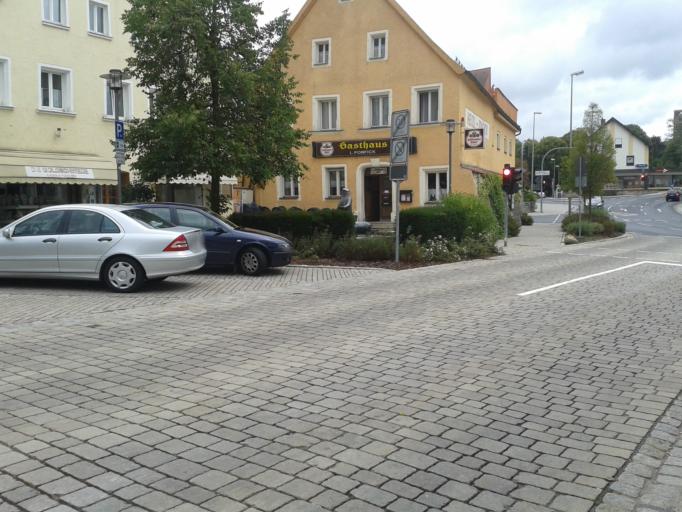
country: DE
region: Bavaria
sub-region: Upper Franconia
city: Pegnitz
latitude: 49.7565
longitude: 11.5434
